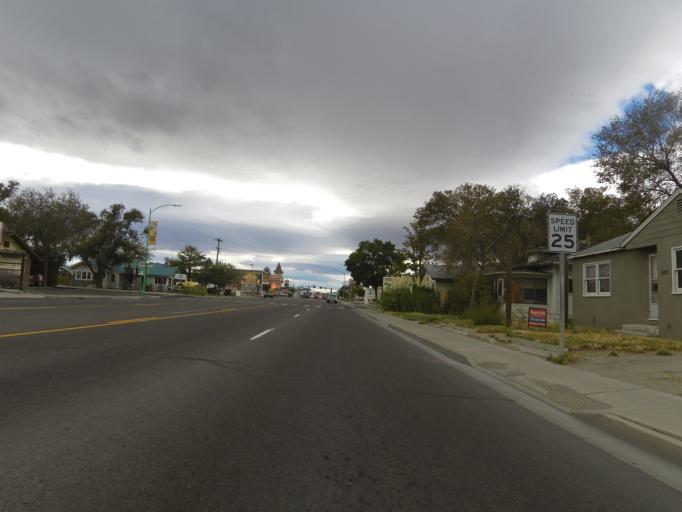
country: US
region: Nevada
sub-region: Churchill County
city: Fallon
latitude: 39.4749
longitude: -118.7846
